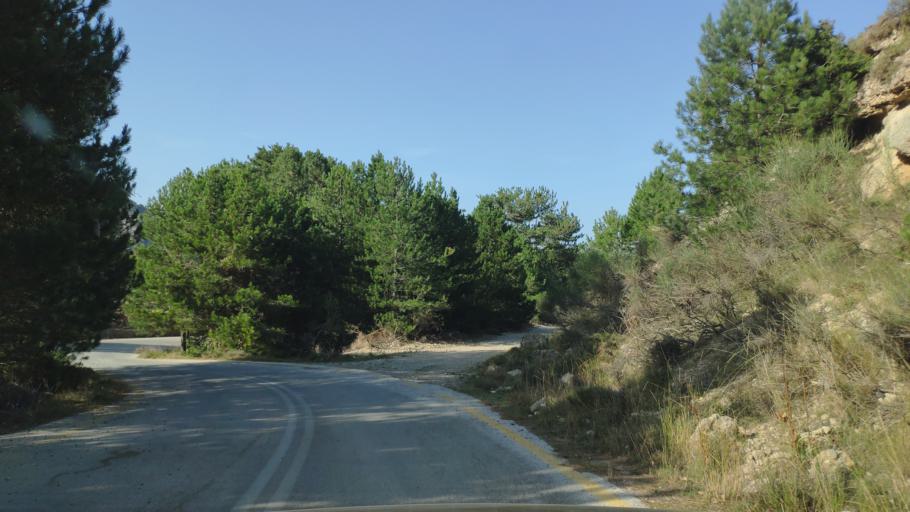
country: GR
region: West Greece
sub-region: Nomos Achaias
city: Aiyira
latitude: 38.0564
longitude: 22.3818
